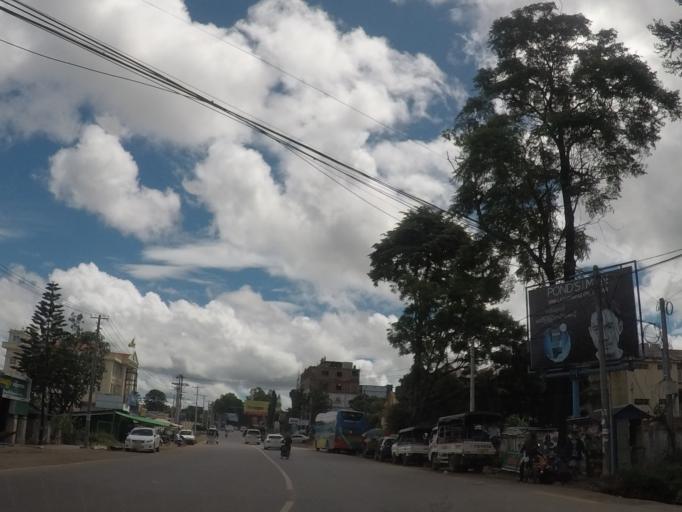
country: MM
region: Mandalay
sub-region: Pyin Oo Lwin District
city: Pyin Oo Lwin
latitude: 22.0361
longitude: 96.4884
